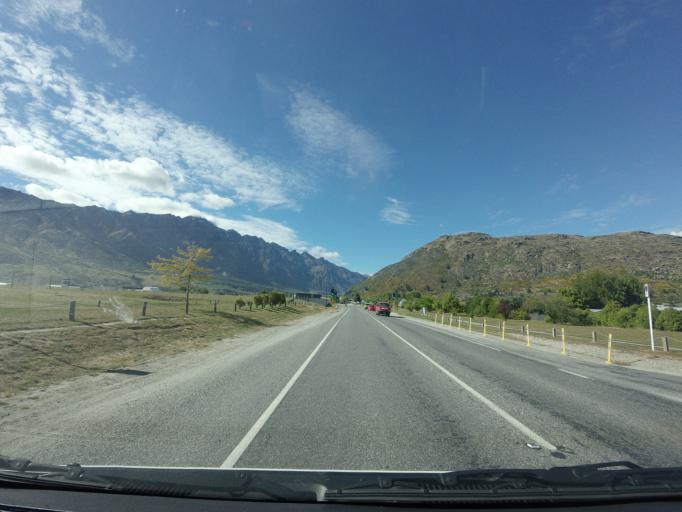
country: NZ
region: Otago
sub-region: Queenstown-Lakes District
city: Queenstown
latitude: -45.0193
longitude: 168.7332
